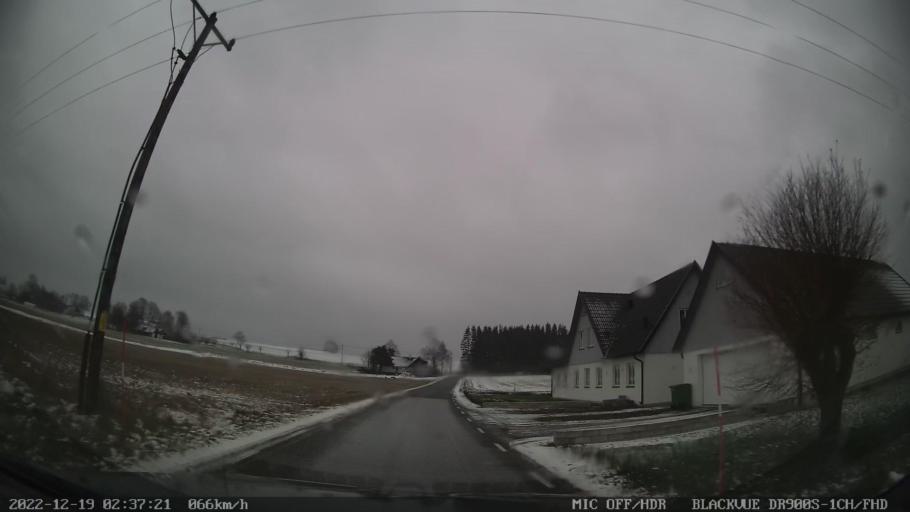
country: SE
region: Skane
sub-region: Tomelilla Kommun
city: Tomelilla
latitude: 55.5185
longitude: 14.0438
